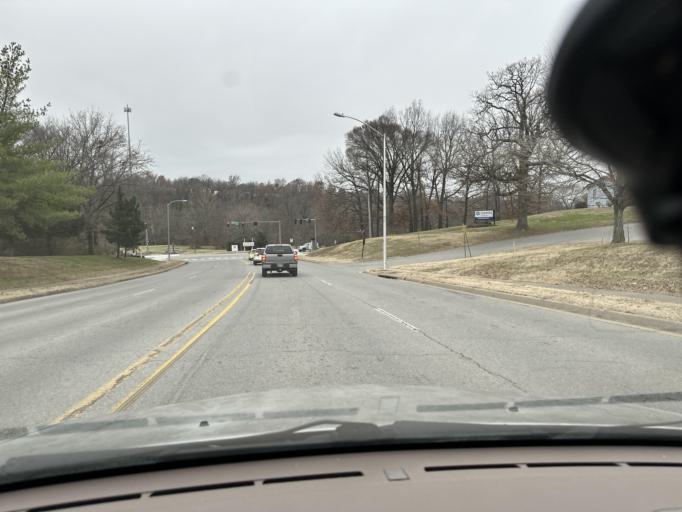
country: US
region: Arkansas
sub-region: Washington County
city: Johnson
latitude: 36.1254
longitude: -94.1612
